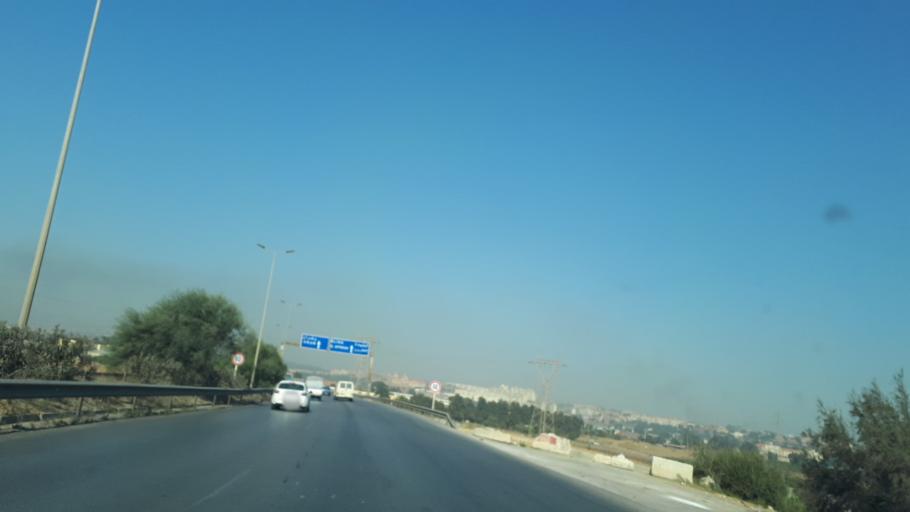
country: DZ
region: Tipaza
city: Baraki
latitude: 36.6829
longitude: 3.1000
